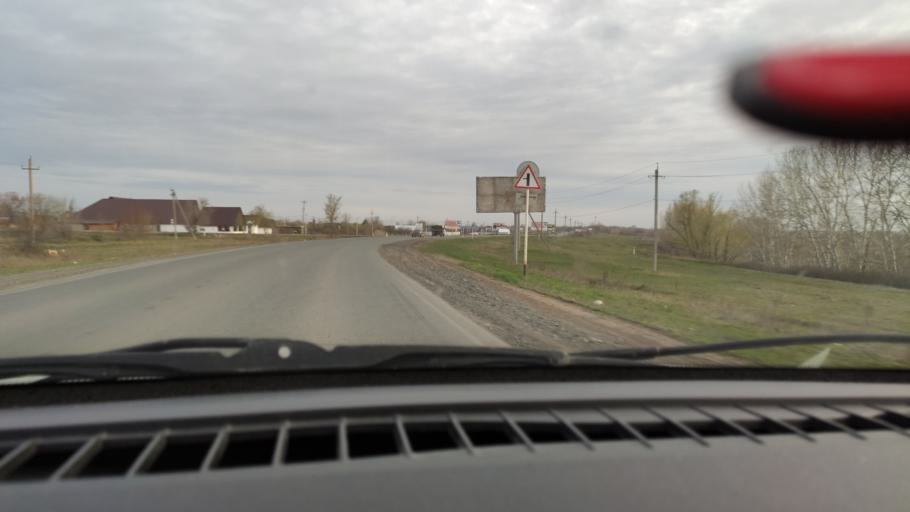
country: RU
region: Orenburg
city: Tatarskaya Kargala
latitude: 51.9040
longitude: 55.1699
